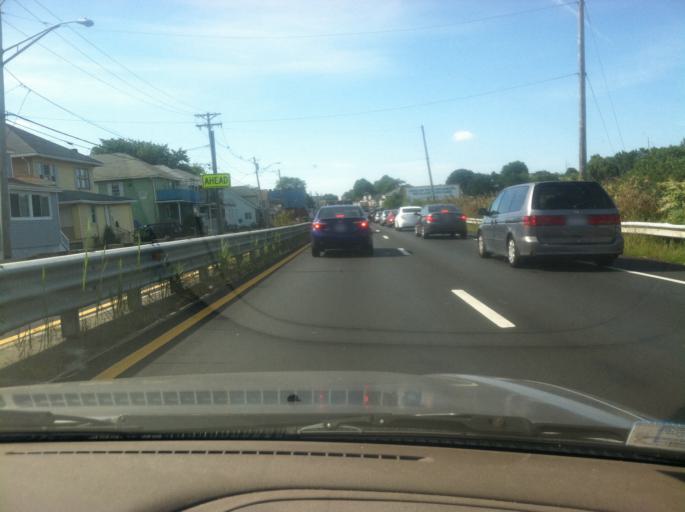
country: US
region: Massachusetts
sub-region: Suffolk County
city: Revere
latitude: 42.4213
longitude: -70.9890
